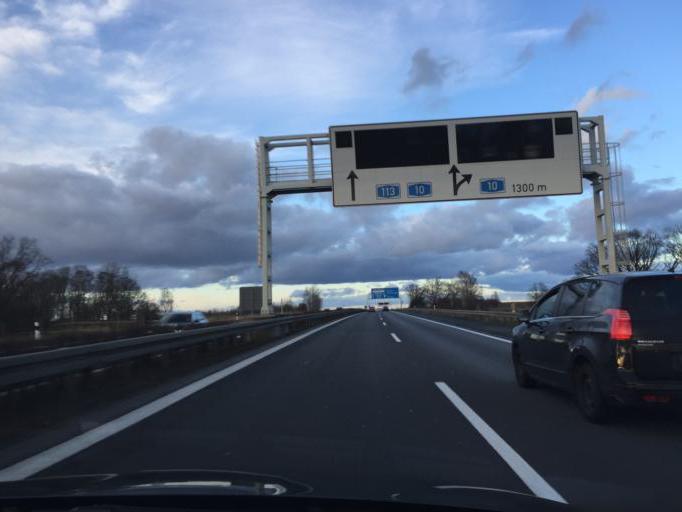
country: DE
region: Brandenburg
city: Mittenwalde
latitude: 52.2992
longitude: 13.5564
